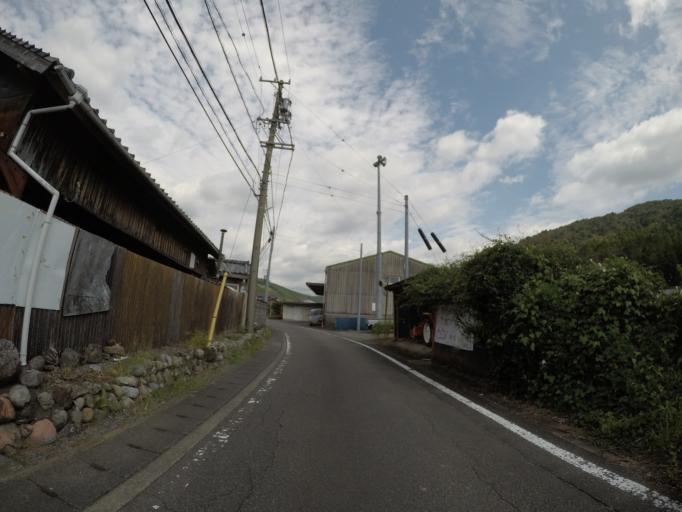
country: JP
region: Shizuoka
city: Kanaya
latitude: 34.8658
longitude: 138.1322
